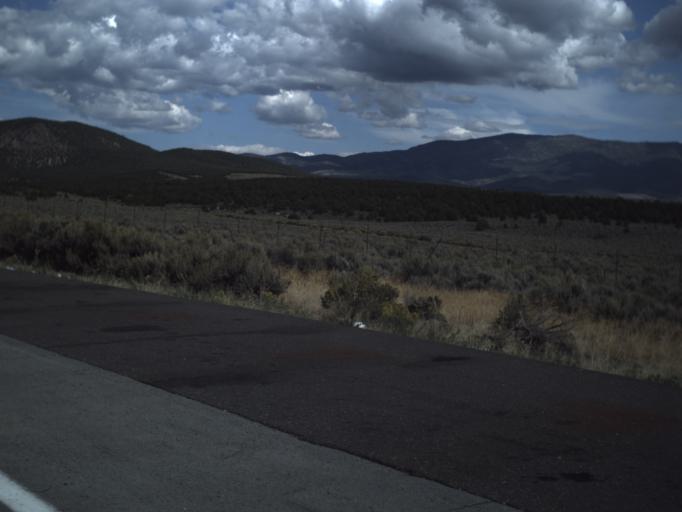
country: US
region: Utah
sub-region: Beaver County
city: Beaver
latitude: 38.1303
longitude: -112.6256
